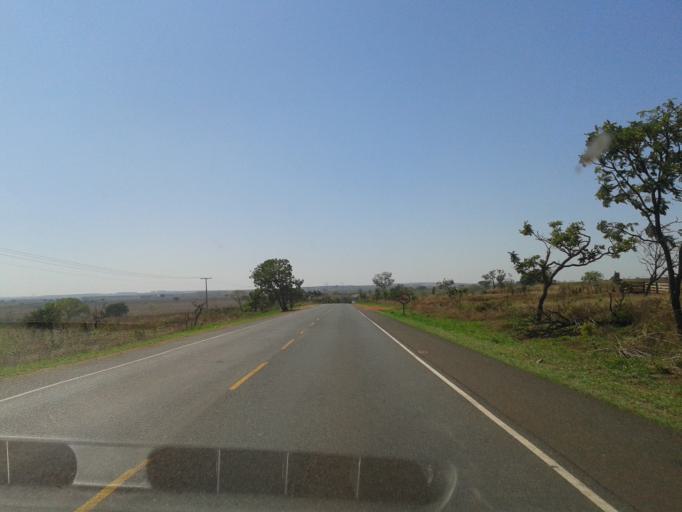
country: BR
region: Minas Gerais
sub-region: Uberlandia
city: Uberlandia
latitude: -19.1155
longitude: -47.9629
